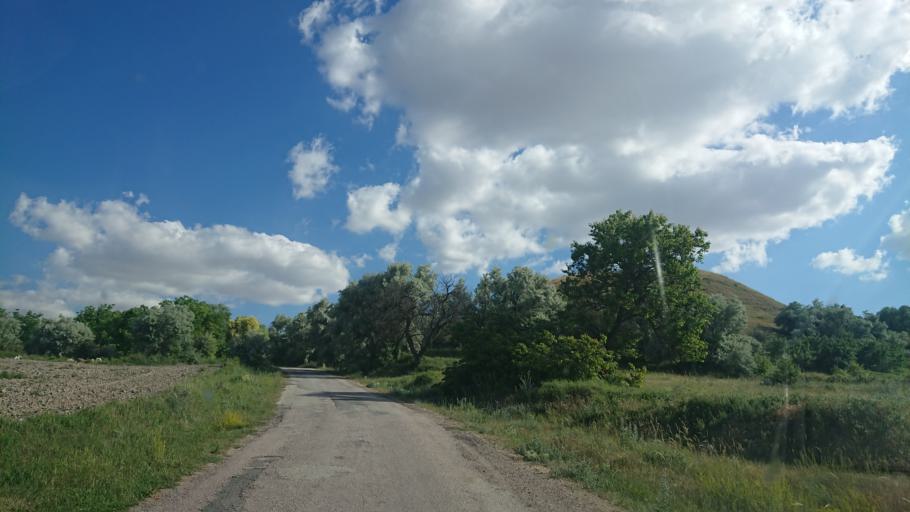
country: TR
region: Aksaray
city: Agacoren
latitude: 38.7561
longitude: 33.8871
